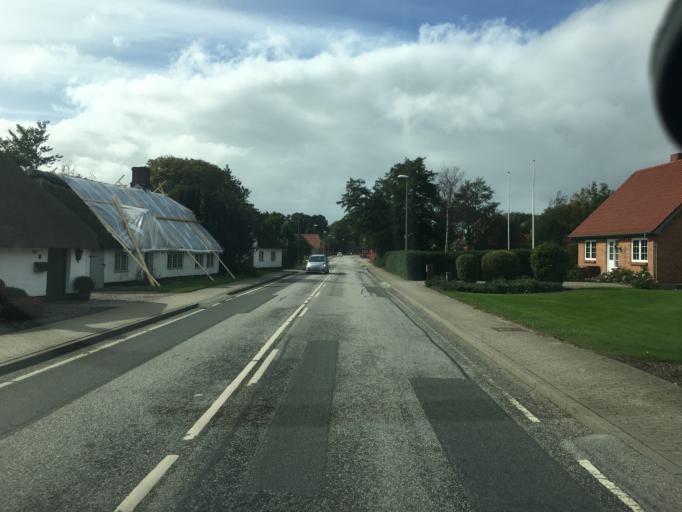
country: DK
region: South Denmark
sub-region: Tonder Kommune
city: Tonder
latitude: 55.0111
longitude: 8.7834
